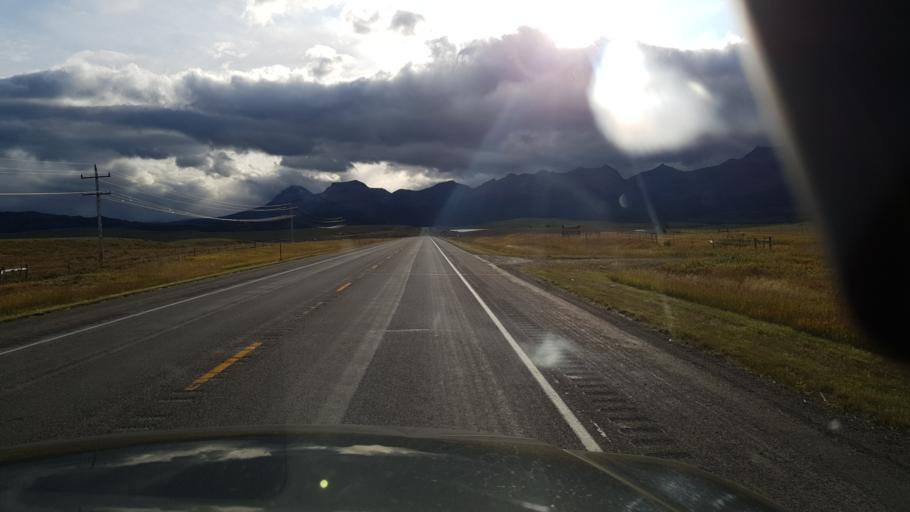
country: US
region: Montana
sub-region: Glacier County
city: South Browning
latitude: 48.4602
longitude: -113.1735
